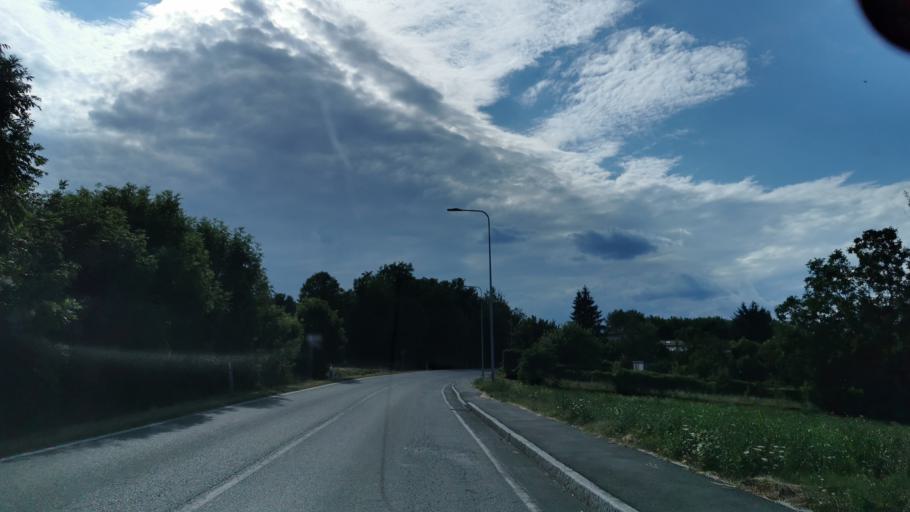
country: IT
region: Lombardy
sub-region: Provincia di Como
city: Anzano del Parco
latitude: 45.7769
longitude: 9.1903
